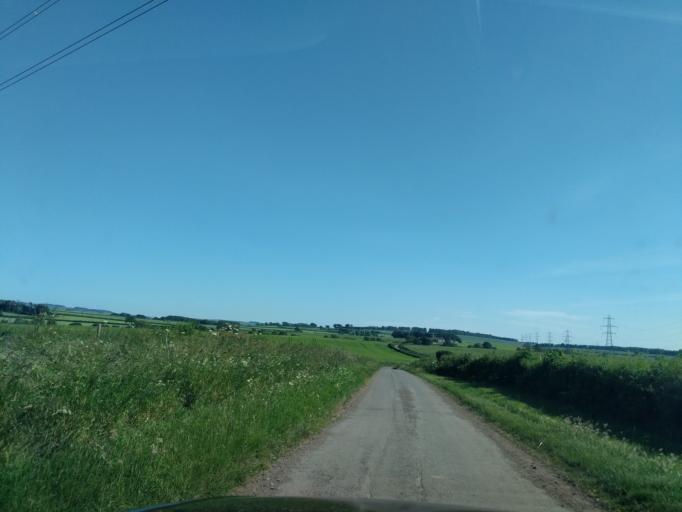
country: GB
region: Scotland
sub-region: East Lothian
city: Ormiston
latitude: 55.8866
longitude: -2.9368
